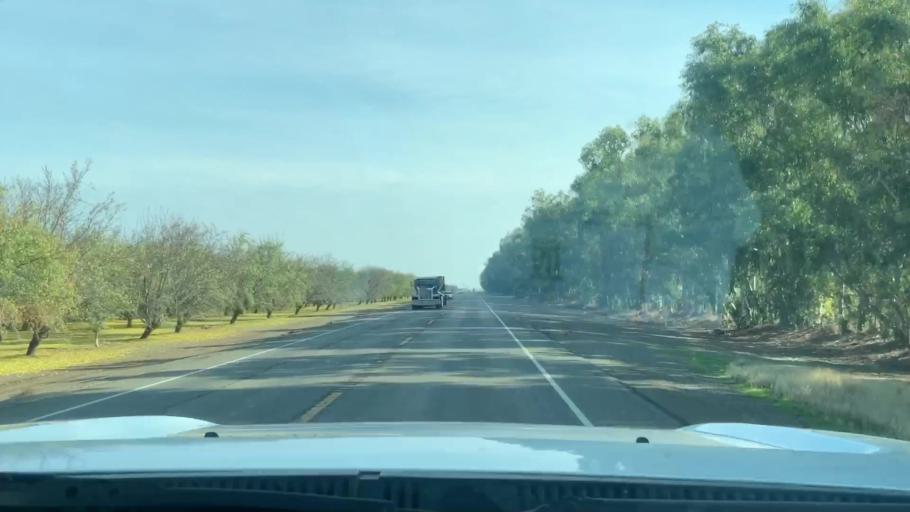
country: US
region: California
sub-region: Fresno County
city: Huron
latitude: 36.2552
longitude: -120.1670
